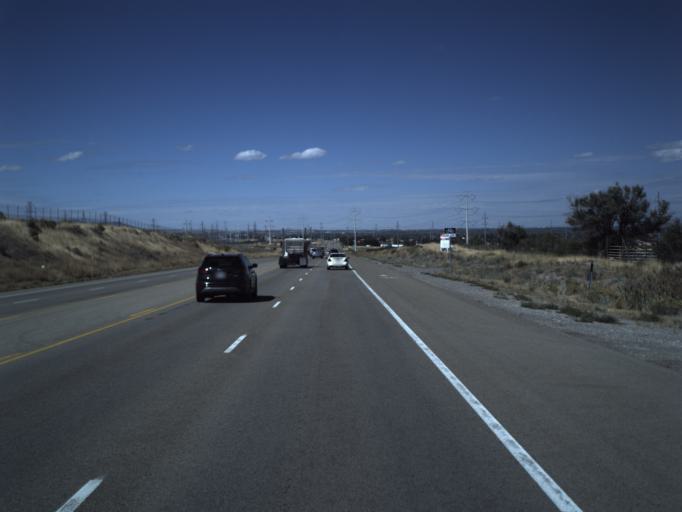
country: US
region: Utah
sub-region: Salt Lake County
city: Bluffdale
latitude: 40.4533
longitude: -111.9383
